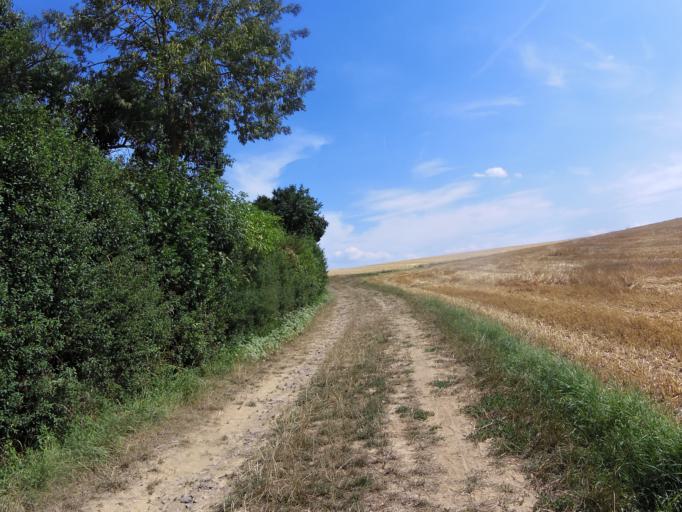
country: DE
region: Bavaria
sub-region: Regierungsbezirk Unterfranken
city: Estenfeld
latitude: 49.8159
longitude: 10.0005
